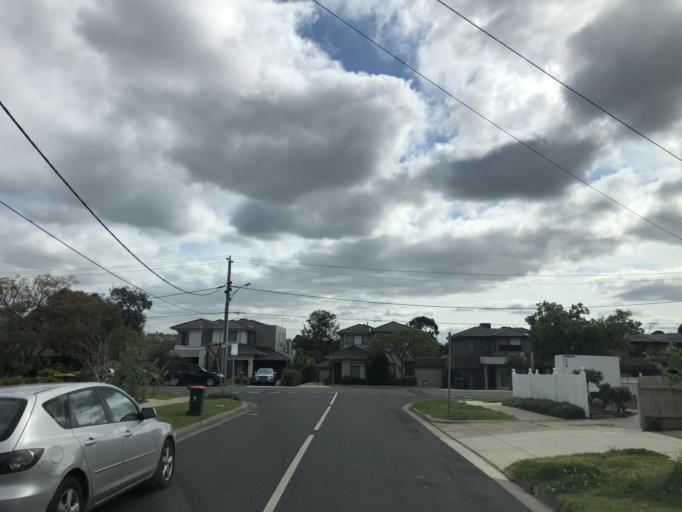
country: AU
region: Victoria
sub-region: Monash
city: Chadstone
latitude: -37.8761
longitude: 145.0951
